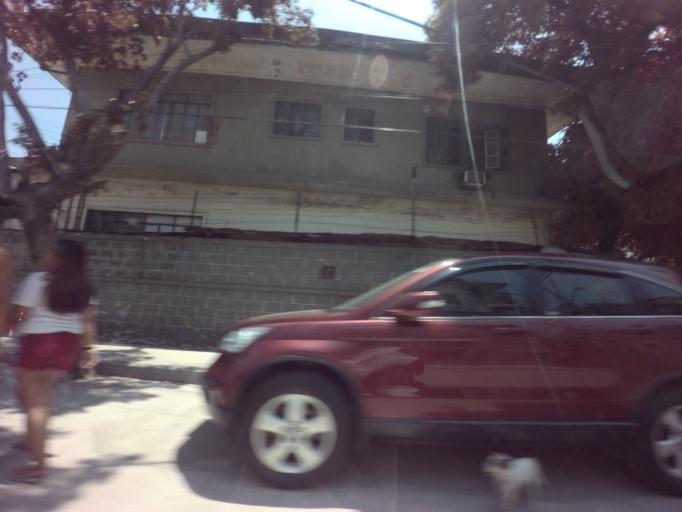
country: PH
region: Metro Manila
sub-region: Makati City
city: Makati City
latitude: 14.5537
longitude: 121.0008
